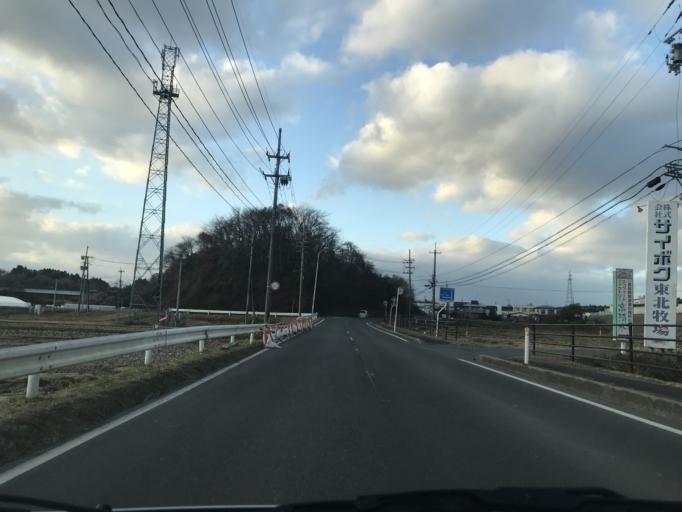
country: JP
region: Miyagi
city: Furukawa
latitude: 38.6662
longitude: 141.0115
